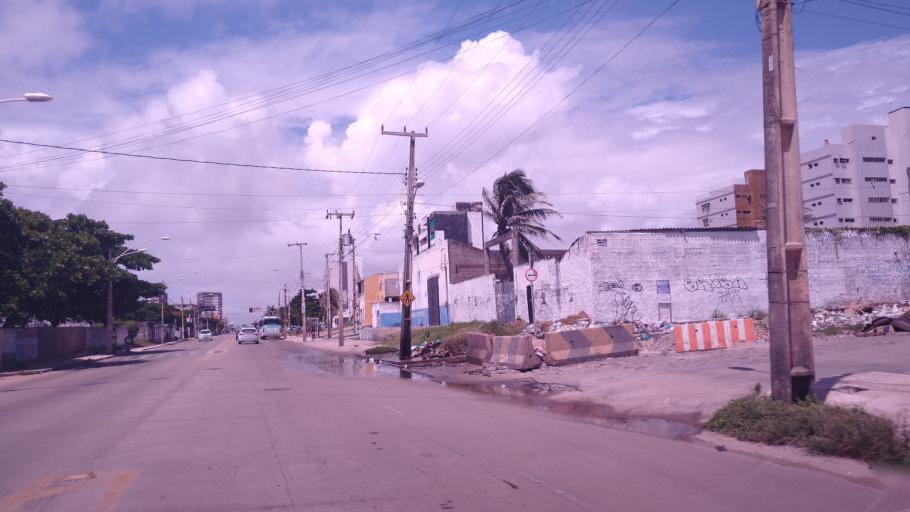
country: BR
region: Ceara
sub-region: Fortaleza
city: Fortaleza
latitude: -3.7244
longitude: -38.4627
